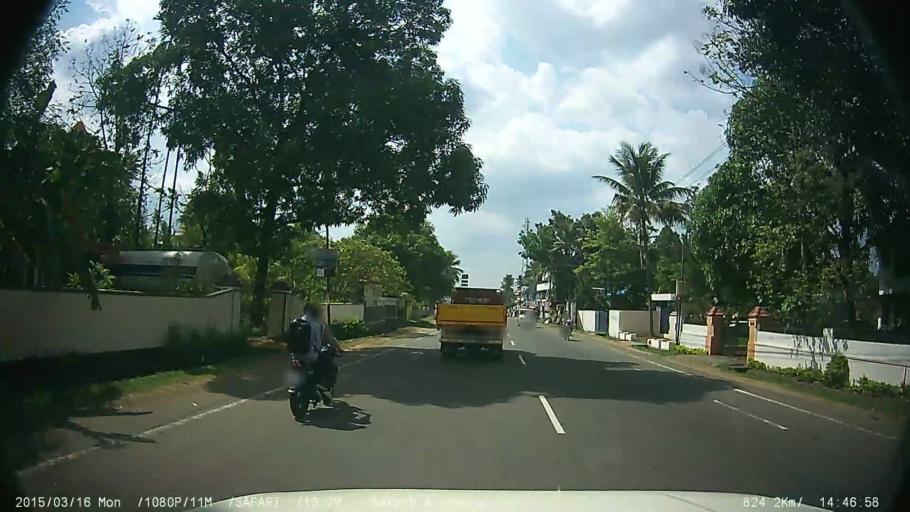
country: IN
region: Kerala
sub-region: Ernakulam
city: Angamali
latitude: 10.1746
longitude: 76.4240
